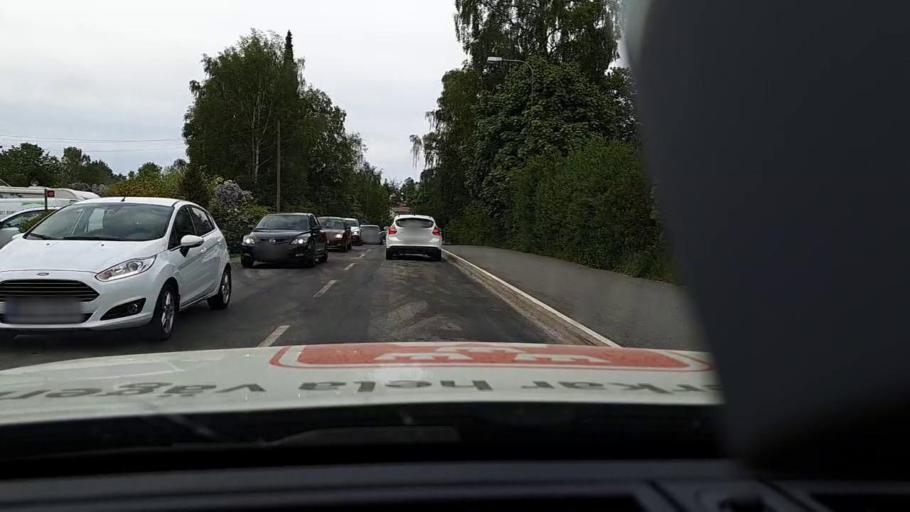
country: SE
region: Stockholm
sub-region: Tyreso Kommun
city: Bollmora
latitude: 59.2156
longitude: 18.2097
